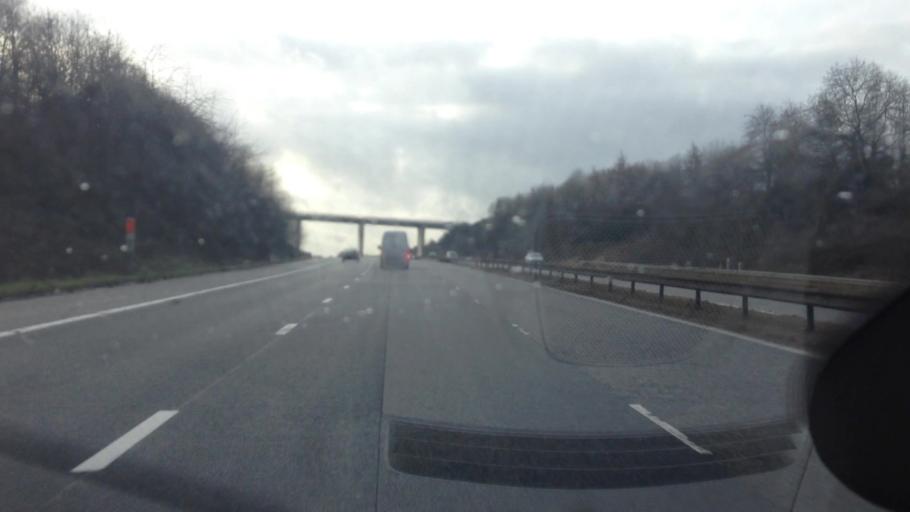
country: GB
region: England
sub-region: City and Borough of Wakefield
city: Crigglestone
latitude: 53.6226
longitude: -1.5469
